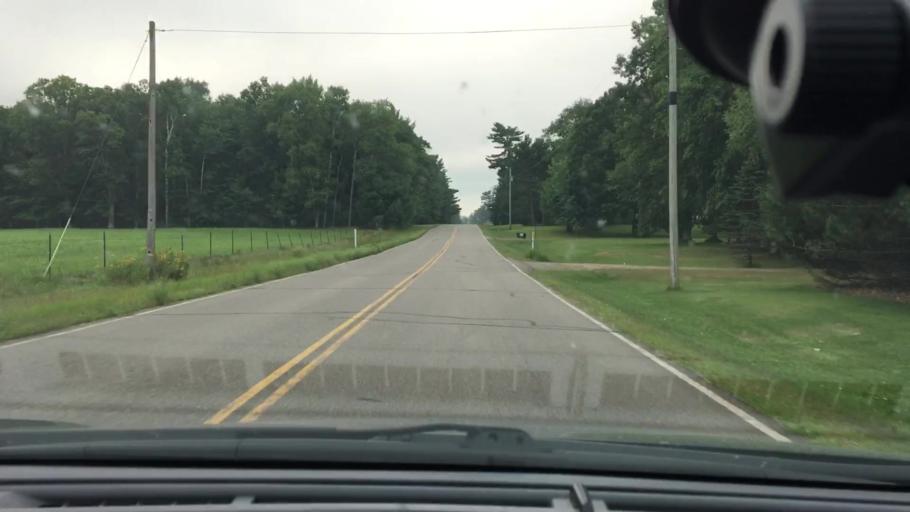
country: US
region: Minnesota
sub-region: Crow Wing County
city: Cross Lake
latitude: 46.6434
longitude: -94.0096
